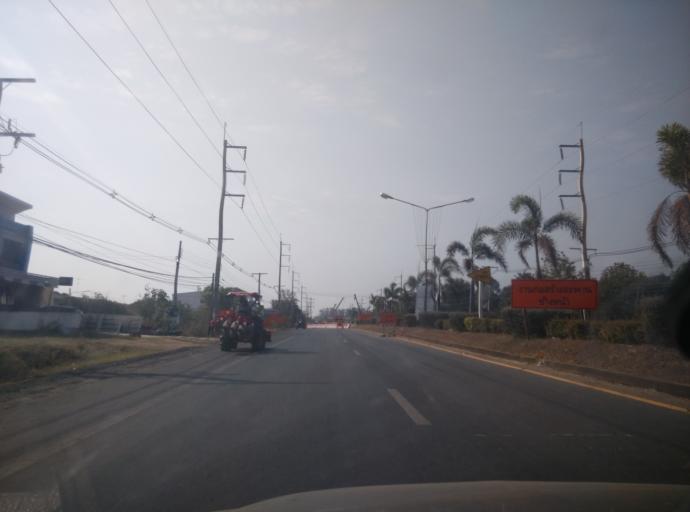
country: TH
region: Sisaket
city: Si Sa Ket
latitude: 15.1252
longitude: 104.2847
